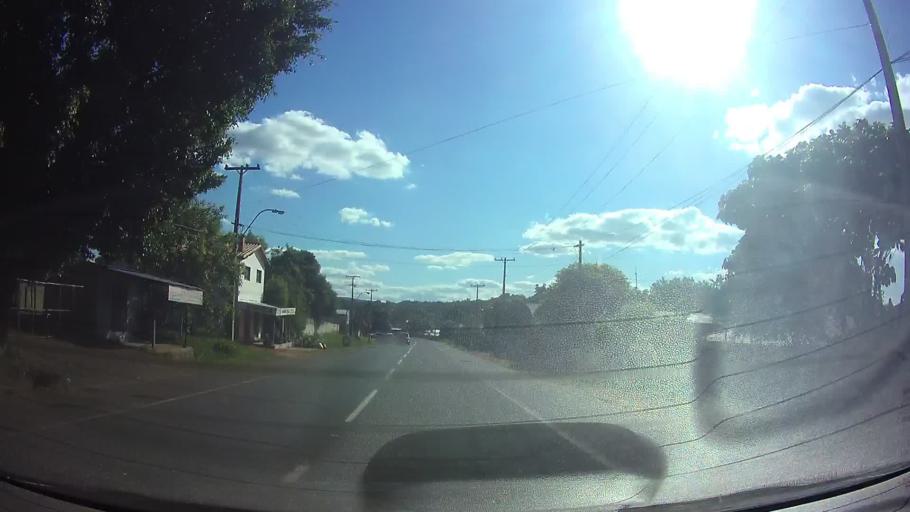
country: PY
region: Cordillera
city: Caacupe
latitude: -25.3844
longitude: -57.1316
